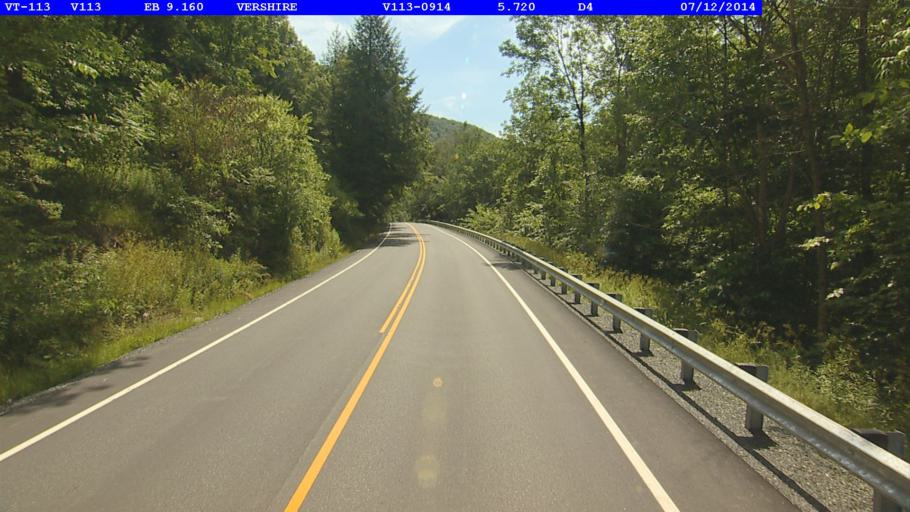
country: US
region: New Hampshire
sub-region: Grafton County
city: Orford
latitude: 43.9603
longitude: -72.2848
